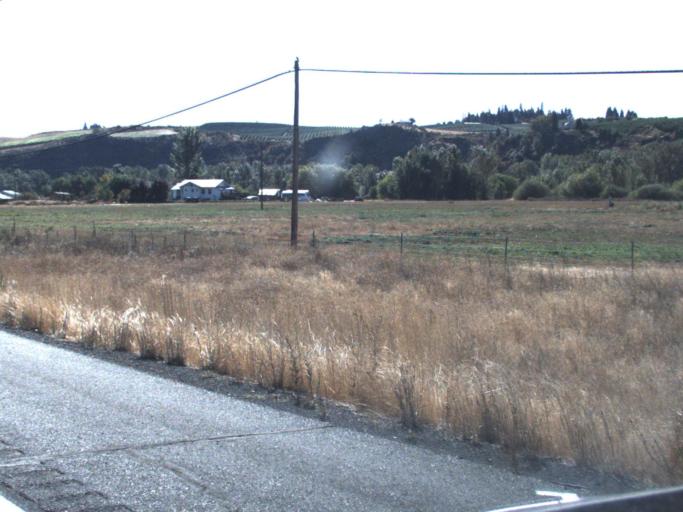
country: US
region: Washington
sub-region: Yakima County
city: Gleed
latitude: 46.6404
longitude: -120.5964
